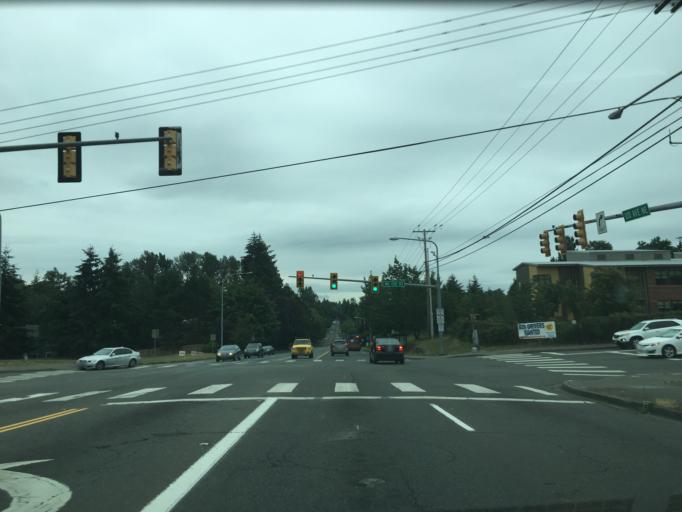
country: US
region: Washington
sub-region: King County
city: Inglewood-Finn Hill
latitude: 47.7188
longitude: -122.2078
